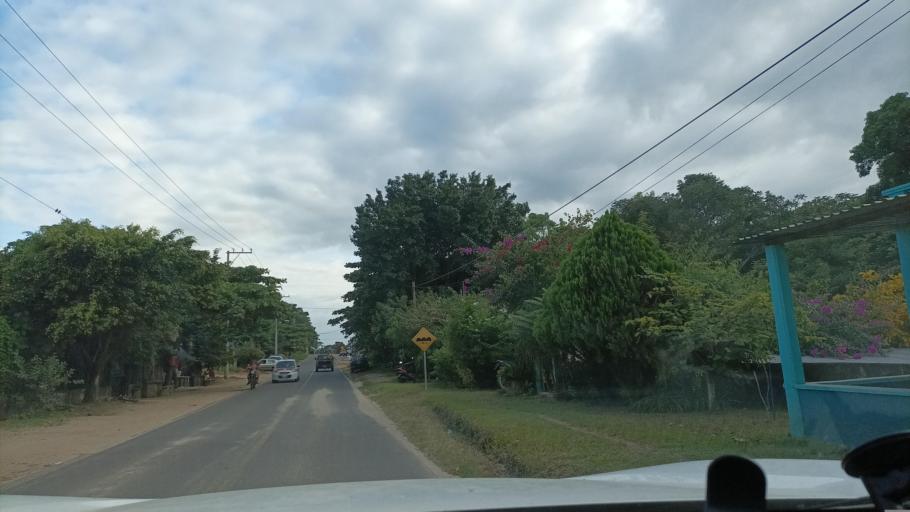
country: MX
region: Veracruz
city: Oluta
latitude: 17.9231
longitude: -94.8882
